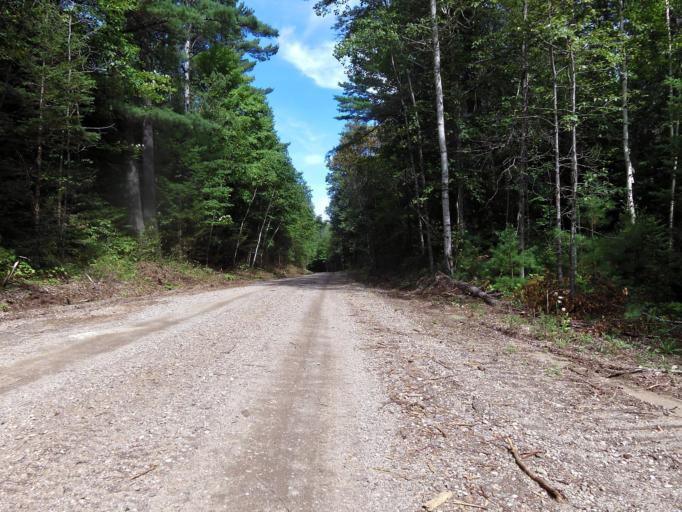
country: CA
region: Ontario
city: Renfrew
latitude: 45.1126
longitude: -76.7246
